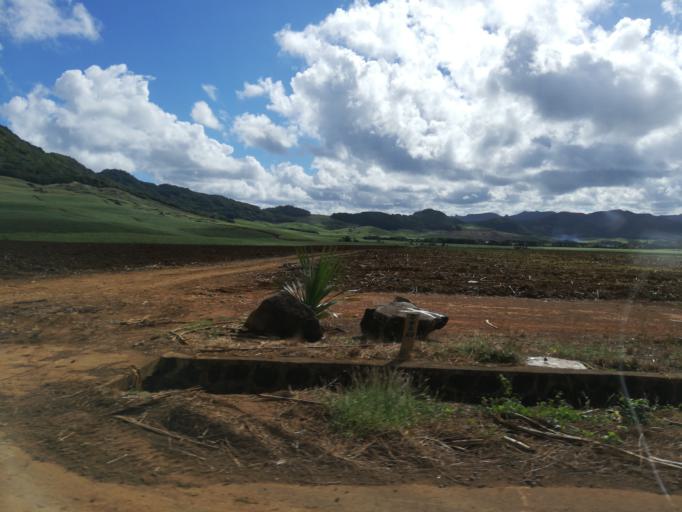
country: MU
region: Grand Port
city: Mahebourg
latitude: -20.3769
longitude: 57.6991
